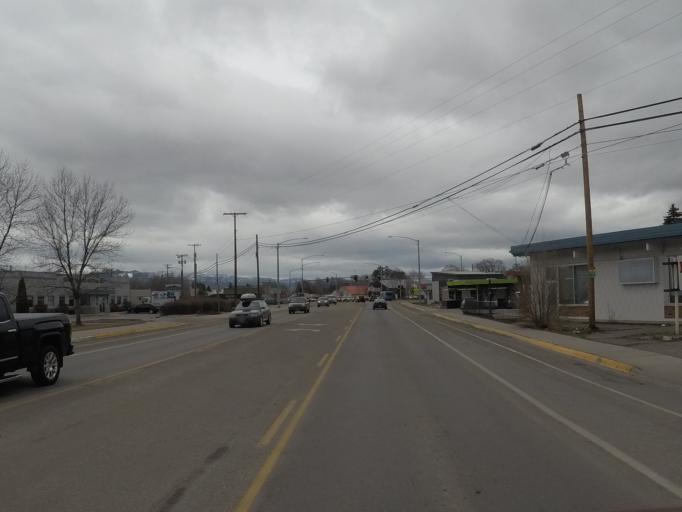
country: US
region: Montana
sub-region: Missoula County
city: Missoula
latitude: 46.8773
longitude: -114.0114
